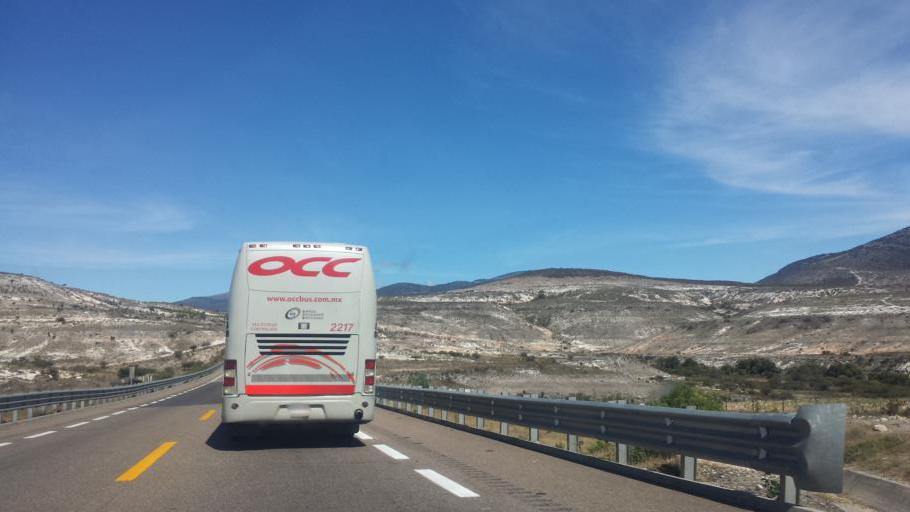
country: MX
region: Oaxaca
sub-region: Villa Tejupam de la Union
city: Villa Tejupam de la Union
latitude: 17.8996
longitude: -97.3679
